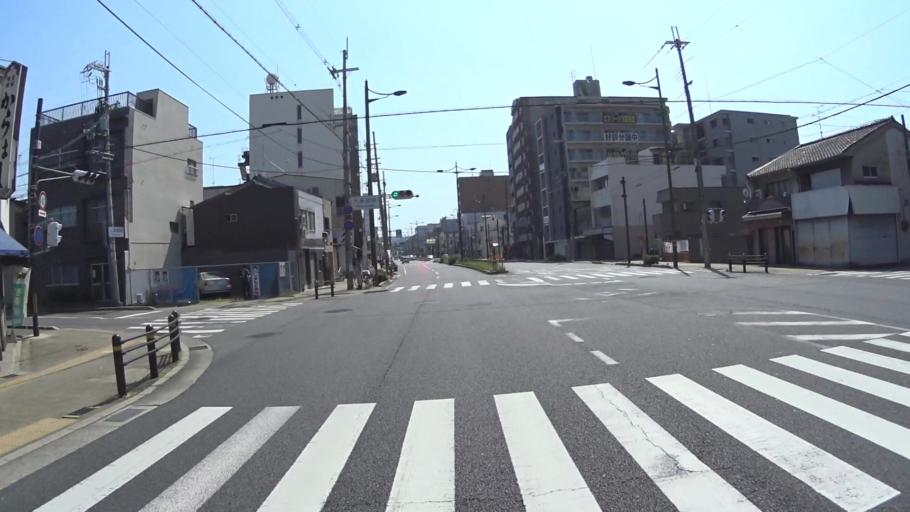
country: JP
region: Kyoto
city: Muko
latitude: 34.9796
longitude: 135.7347
